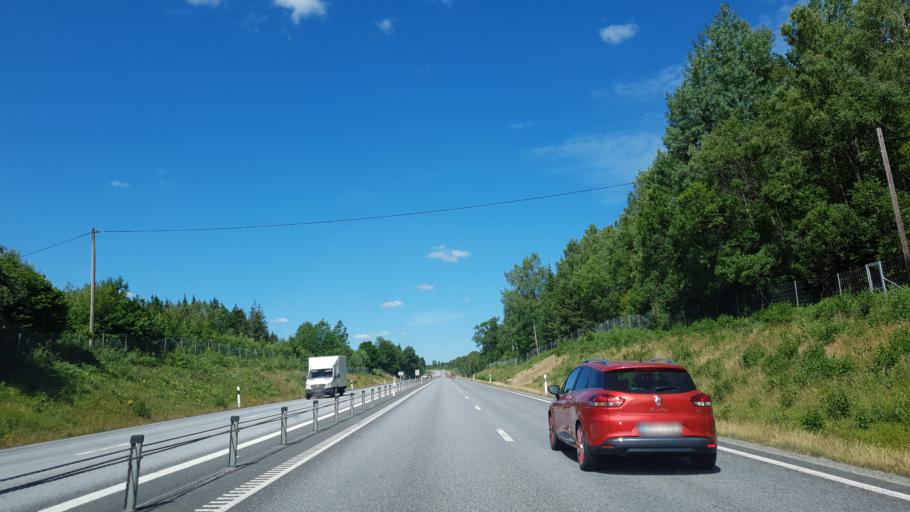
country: SE
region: Kronoberg
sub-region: Vaxjo Kommun
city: Gemla
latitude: 56.8999
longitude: 14.6760
